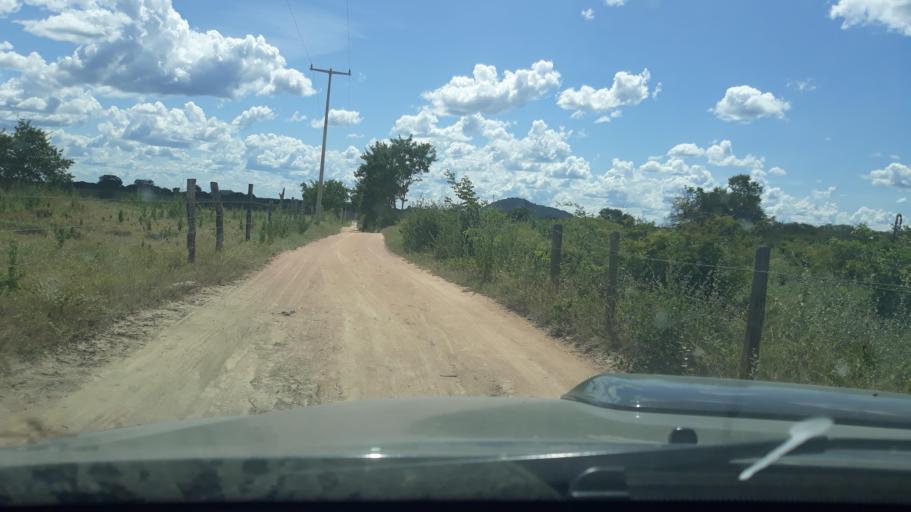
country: BR
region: Bahia
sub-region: Riacho De Santana
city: Riacho de Santana
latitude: -13.8638
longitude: -43.0205
